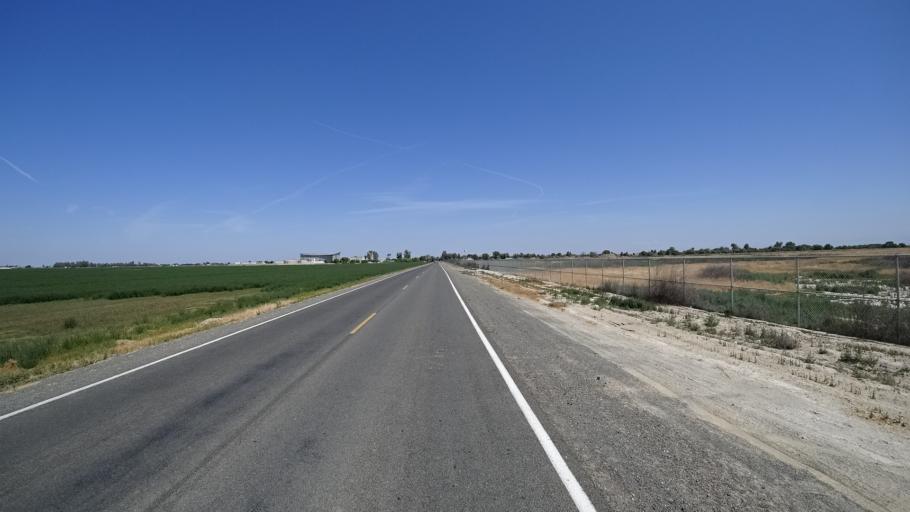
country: US
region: California
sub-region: Kings County
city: Stratford
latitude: 36.2270
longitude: -119.7625
